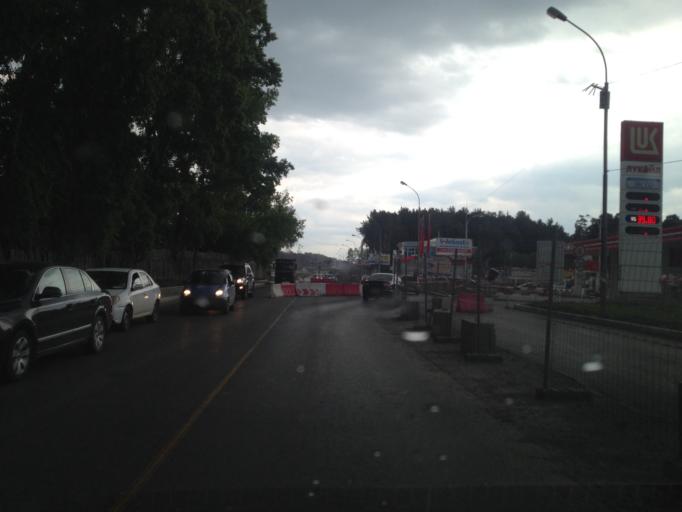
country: RU
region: Sverdlovsk
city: Sovkhoznyy
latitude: 56.7972
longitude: 60.5956
